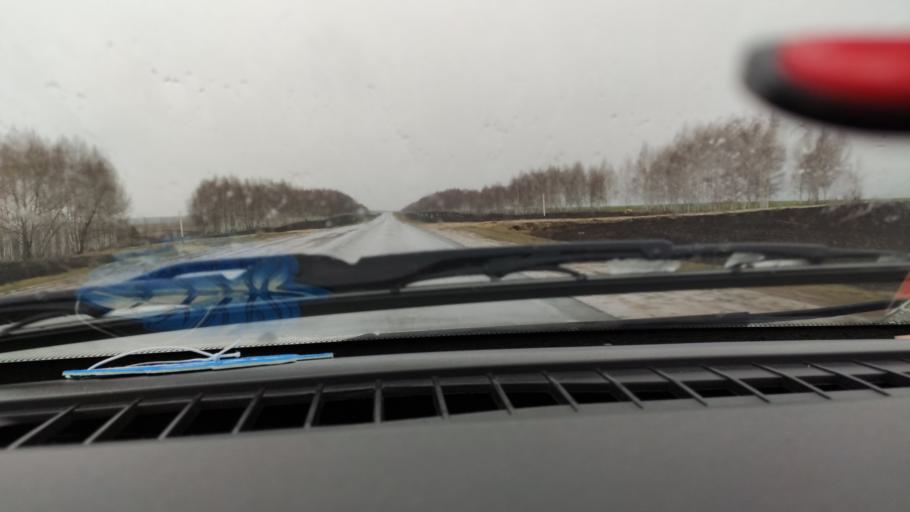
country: RU
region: Samara
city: Chelno-Vershiny
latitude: 54.6824
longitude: 51.0848
